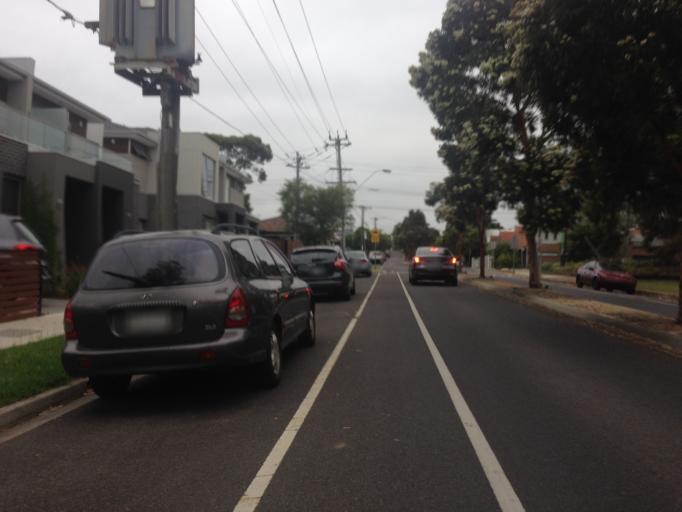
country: AU
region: Victoria
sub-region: Darebin
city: Thornbury
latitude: -37.7546
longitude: 145.0061
